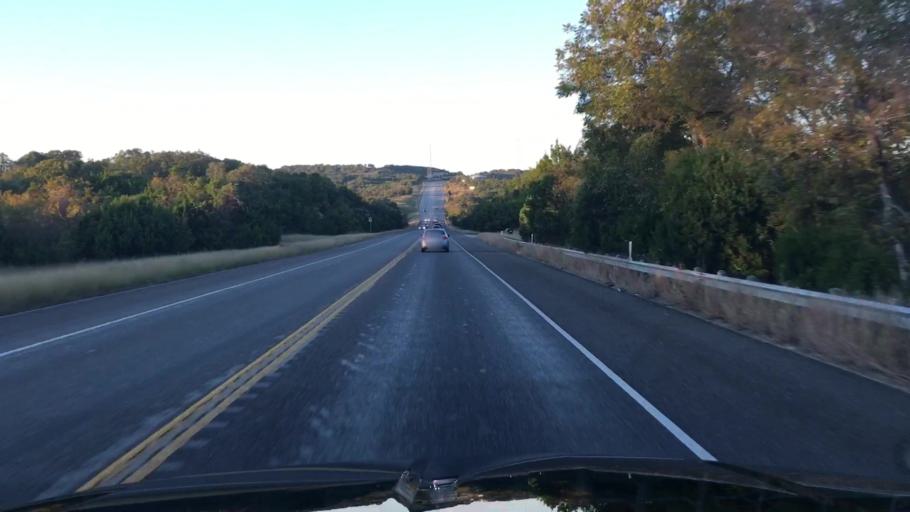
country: US
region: Texas
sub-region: Blanco County
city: Blanco
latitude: 29.9466
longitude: -98.4103
